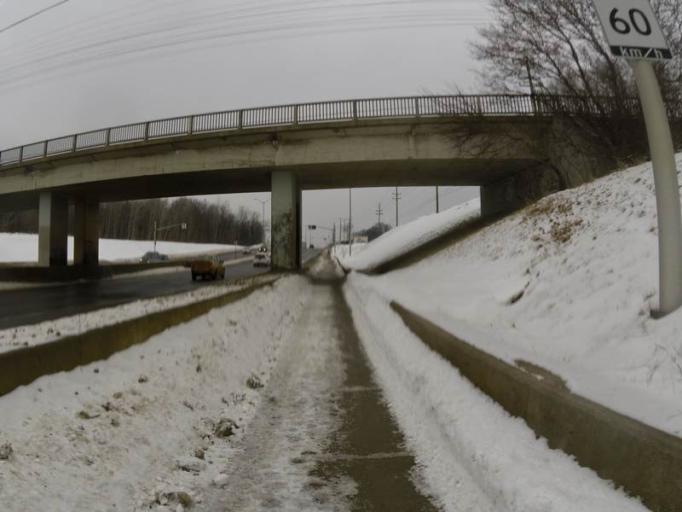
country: CA
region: Ontario
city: Bells Corners
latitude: 45.3366
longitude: -75.7534
